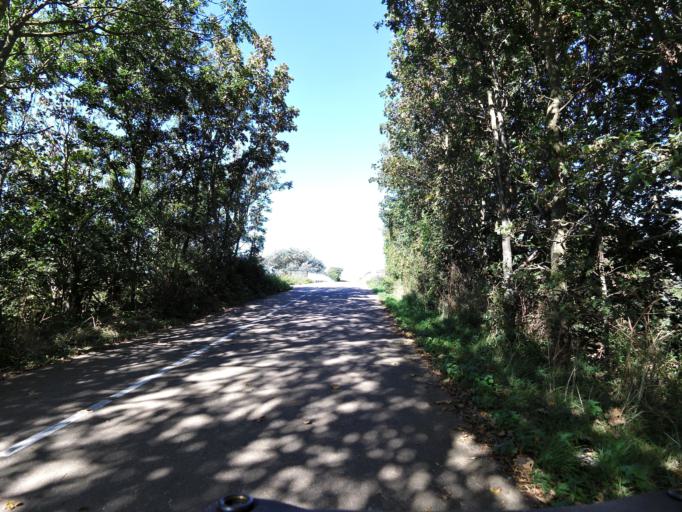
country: NL
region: South Holland
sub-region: Gemeente Goeree-Overflakkee
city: Ouddorp
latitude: 51.8238
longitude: 3.9181
